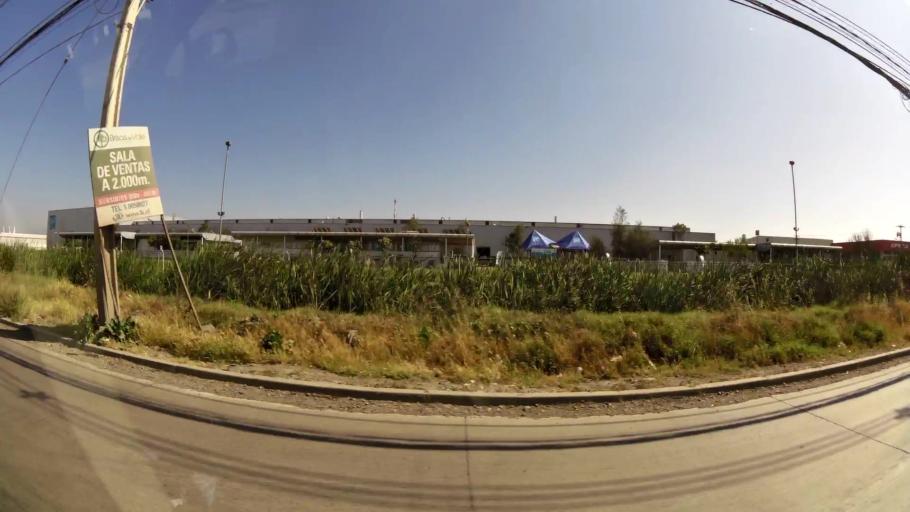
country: CL
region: Santiago Metropolitan
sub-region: Provincia de Chacabuco
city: Chicureo Abajo
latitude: -33.3185
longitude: -70.7331
